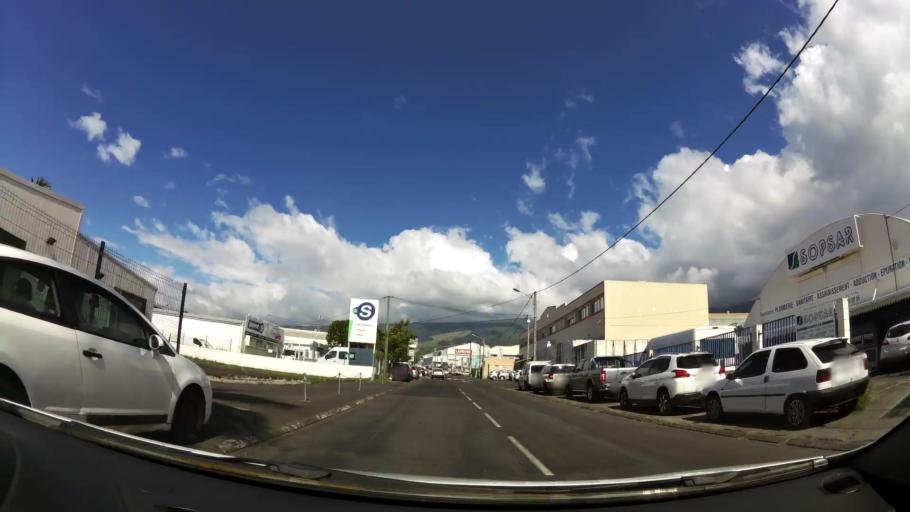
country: RE
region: Reunion
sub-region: Reunion
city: Saint-Denis
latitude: -20.8943
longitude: 55.4961
